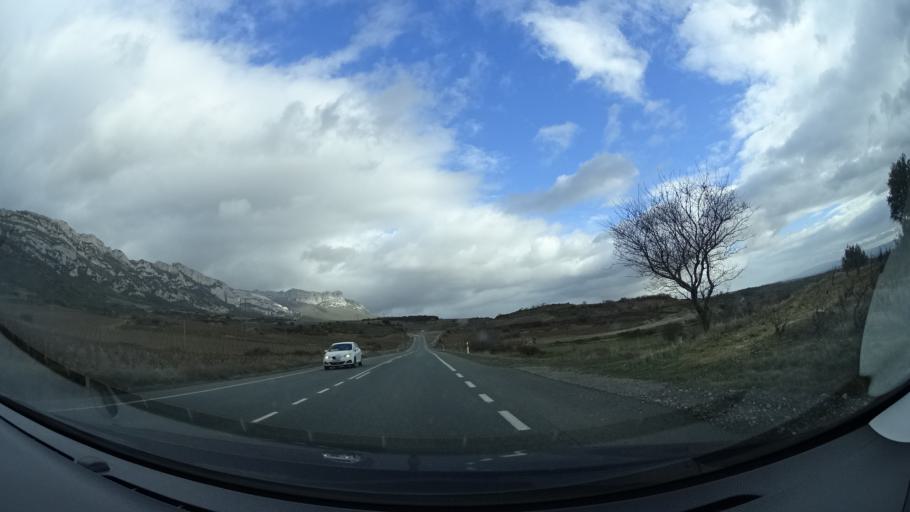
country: ES
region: Basque Country
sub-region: Provincia de Alava
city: Samaniego
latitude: 42.5697
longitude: -2.6720
